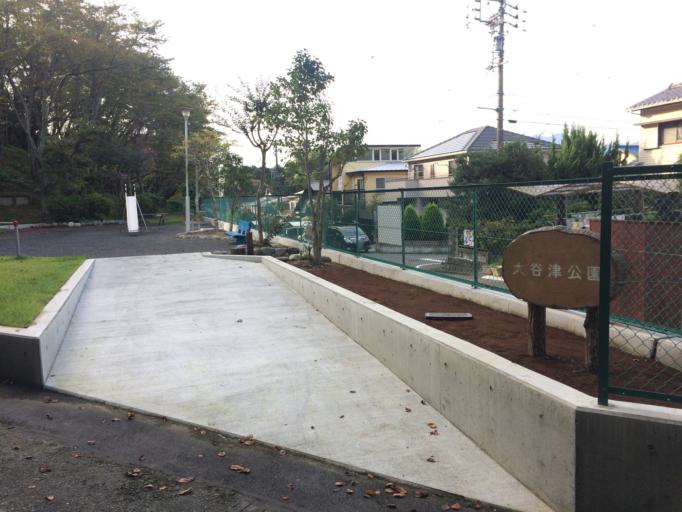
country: JP
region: Shizuoka
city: Shizuoka-shi
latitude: 34.9956
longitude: 138.4579
